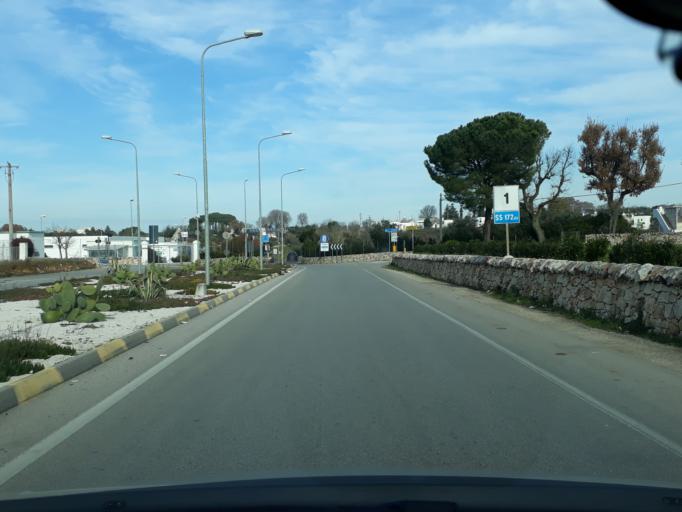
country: IT
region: Apulia
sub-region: Provincia di Bari
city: Locorotondo
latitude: 40.7637
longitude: 17.3316
